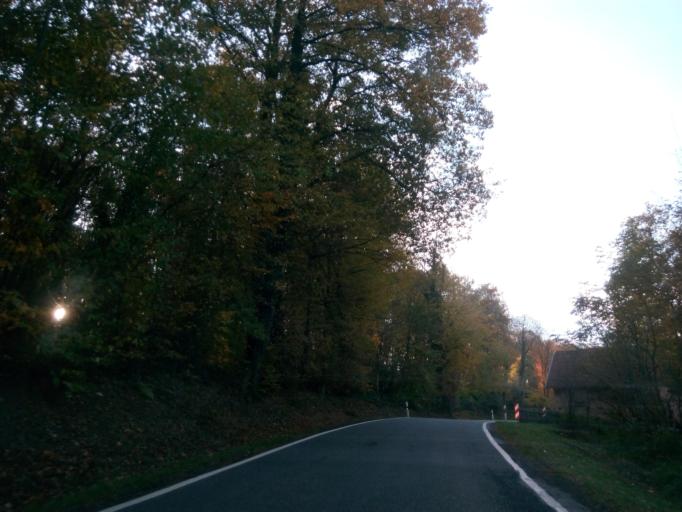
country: DE
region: Saarland
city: Saarbrucken
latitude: 49.2900
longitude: 6.9883
